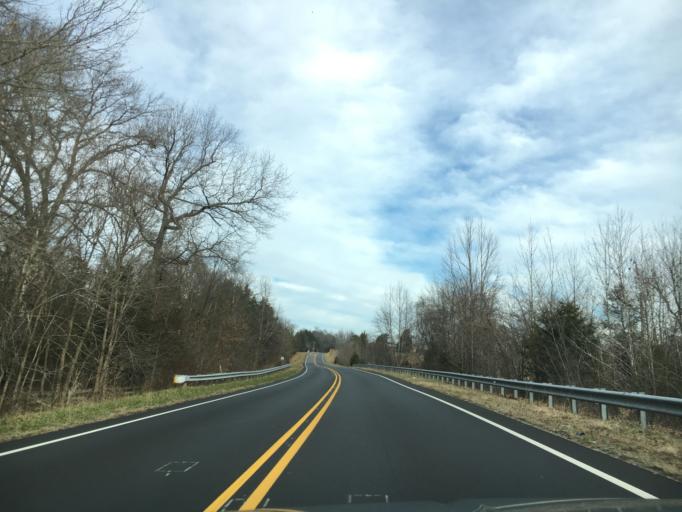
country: US
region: Virginia
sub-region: Goochland County
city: Goochland
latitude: 37.7929
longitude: -77.8727
